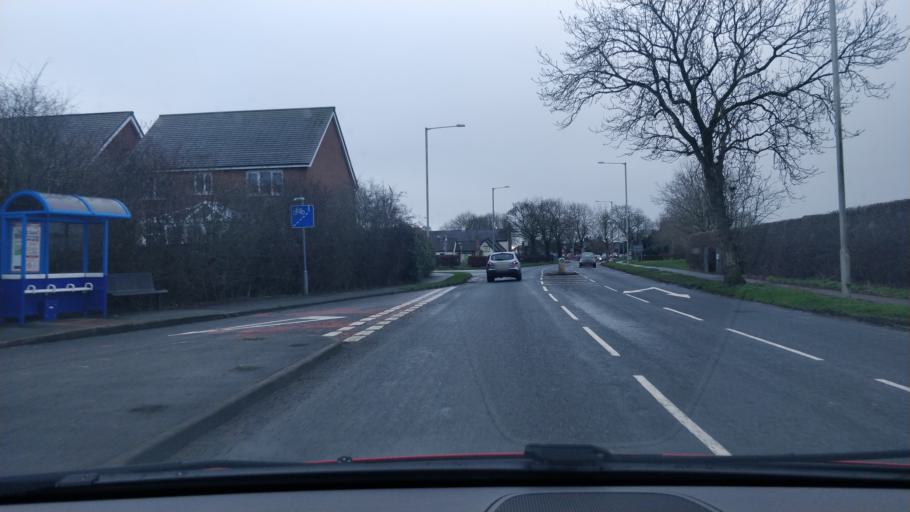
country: GB
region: England
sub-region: Lancashire
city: Tarleton
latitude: 53.7090
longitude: -2.7932
